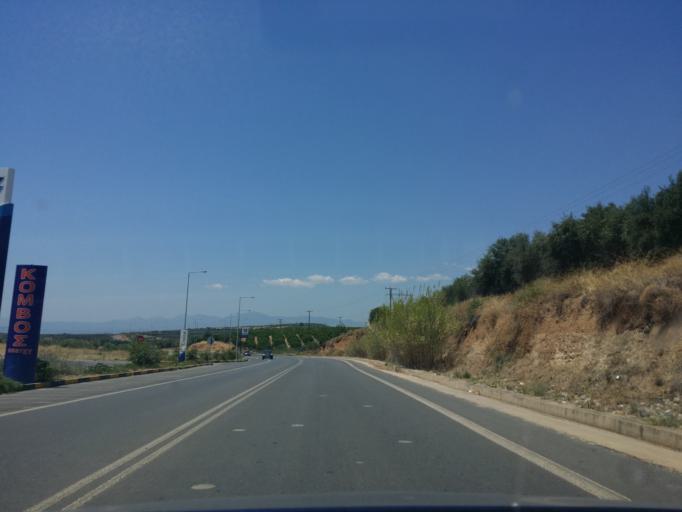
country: GR
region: Peloponnese
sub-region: Nomos Lakonias
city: Kato Glikovrisi
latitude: 36.8573
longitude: 22.7835
